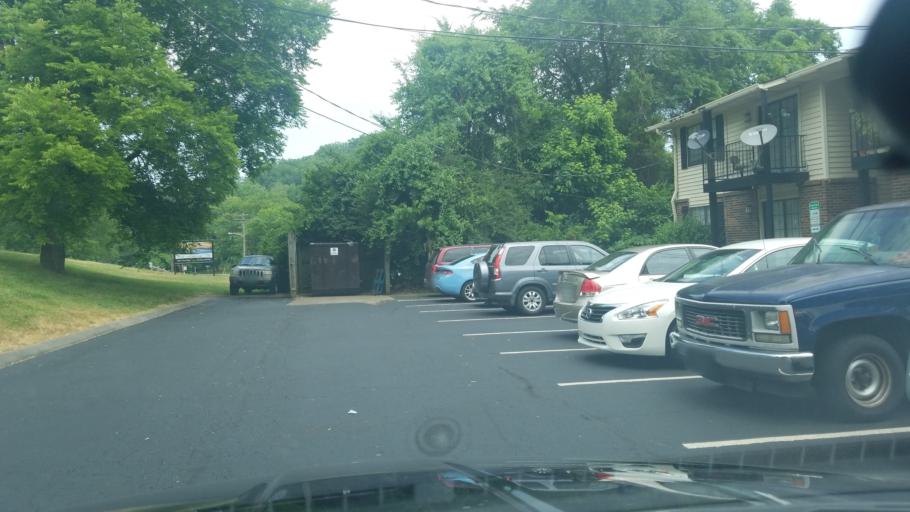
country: US
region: Tennessee
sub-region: Davidson County
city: Goodlettsville
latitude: 36.2530
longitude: -86.7435
